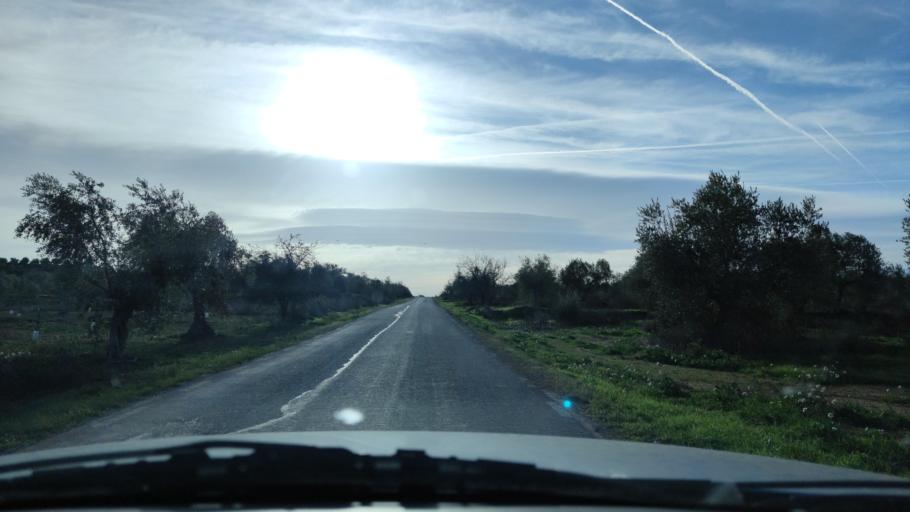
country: ES
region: Catalonia
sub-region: Provincia de Lleida
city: Aspa
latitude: 41.4876
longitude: 0.6753
